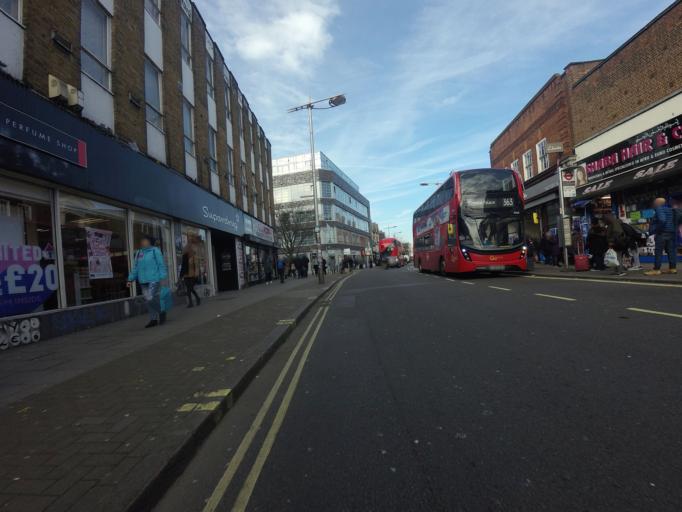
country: GB
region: England
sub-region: Greater London
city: Camberwell
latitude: 51.4714
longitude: -0.0696
